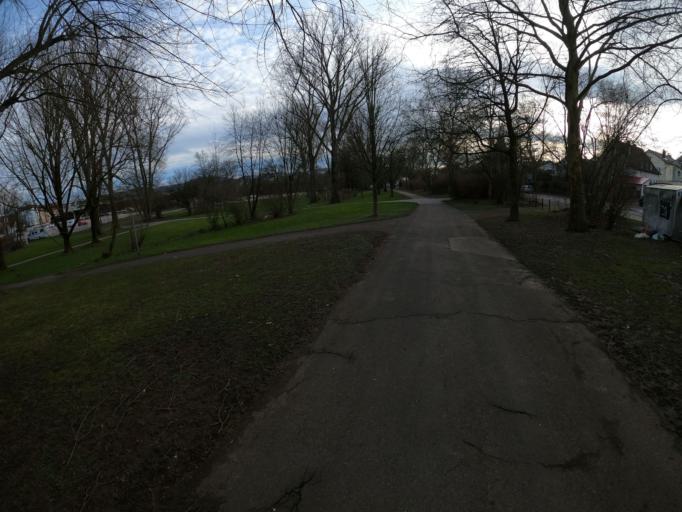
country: DE
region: Baden-Wuerttemberg
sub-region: Regierungsbezirk Stuttgart
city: Goeppingen
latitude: 48.7125
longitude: 9.6464
